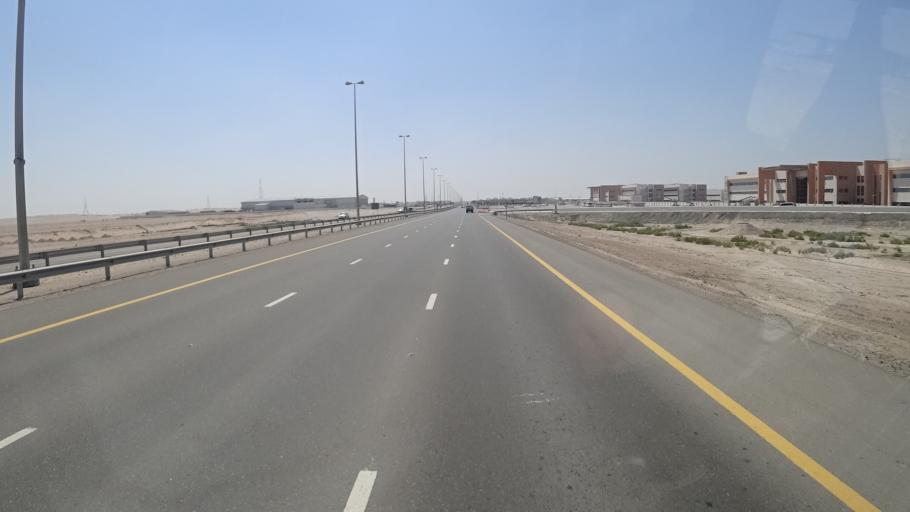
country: AE
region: Abu Dhabi
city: Abu Dhabi
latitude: 24.3149
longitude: 54.6792
